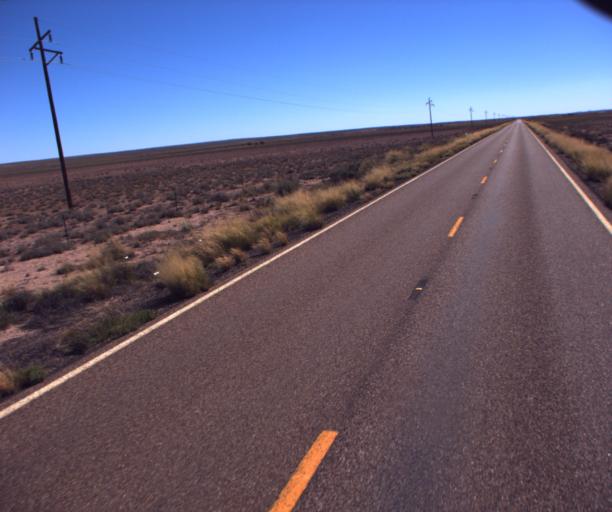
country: US
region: Arizona
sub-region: Navajo County
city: Holbrook
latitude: 35.0985
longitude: -110.0961
